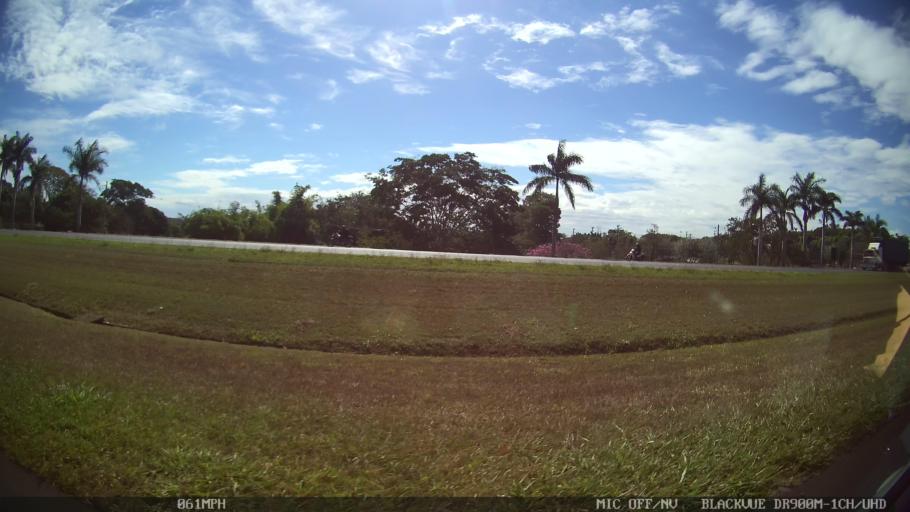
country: BR
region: Sao Paulo
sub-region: Sao Jose Do Rio Preto
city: Sao Jose do Rio Preto
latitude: -20.8161
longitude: -49.4453
